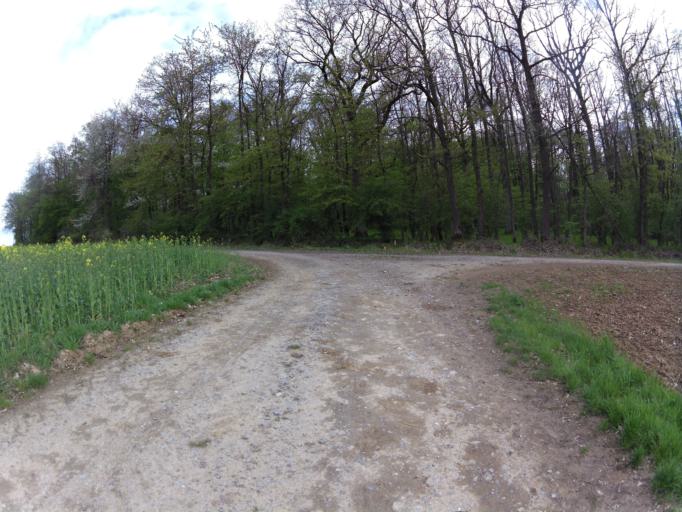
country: DE
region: Bavaria
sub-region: Regierungsbezirk Unterfranken
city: Prosselsheim
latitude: 49.8618
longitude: 10.1519
